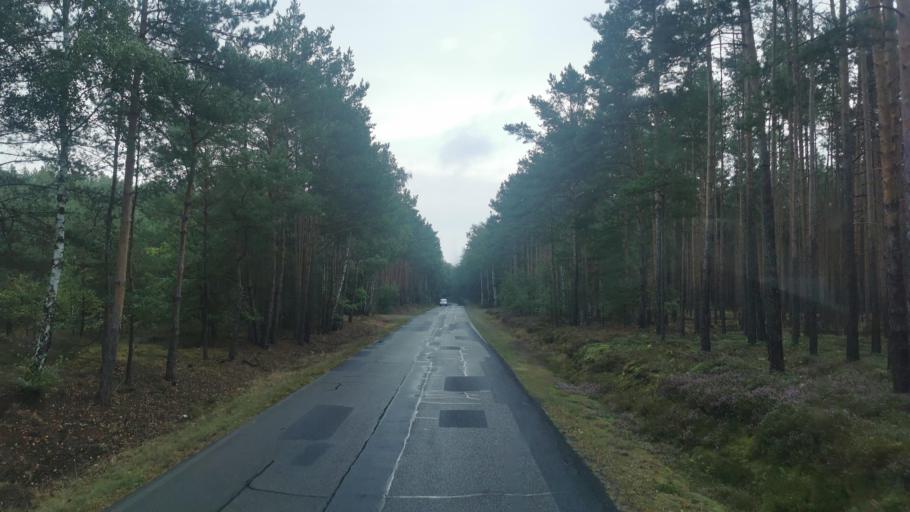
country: DE
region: Brandenburg
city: Kolkwitz
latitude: 51.7322
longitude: 14.2403
